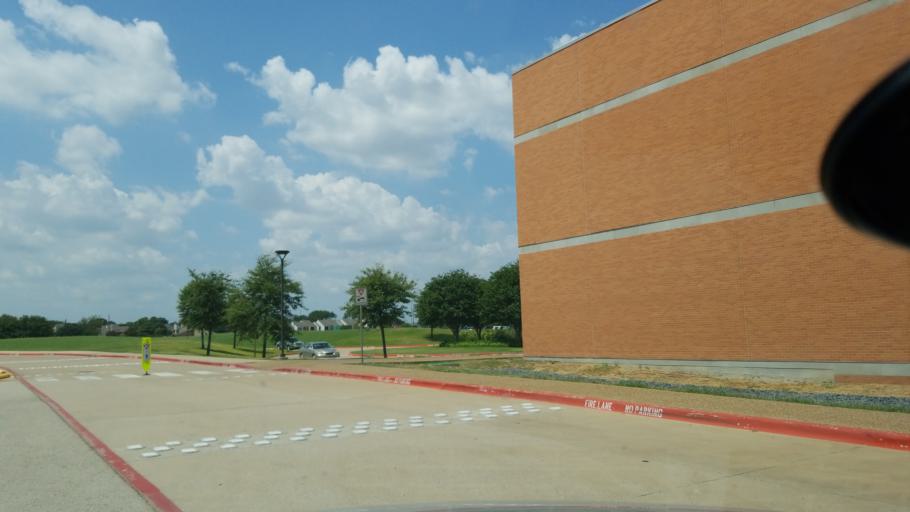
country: US
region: Texas
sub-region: Dallas County
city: Richardson
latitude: 32.9212
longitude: -96.7319
